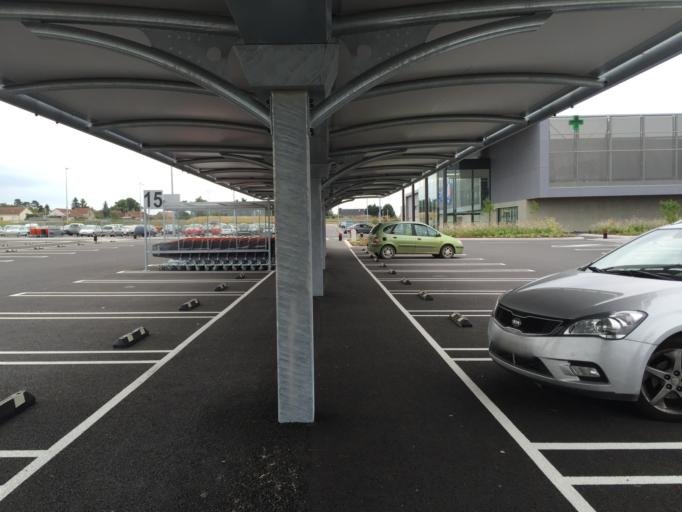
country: FR
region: Auvergne
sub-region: Departement de l'Allier
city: Moulins
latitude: 46.5896
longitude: 3.3304
